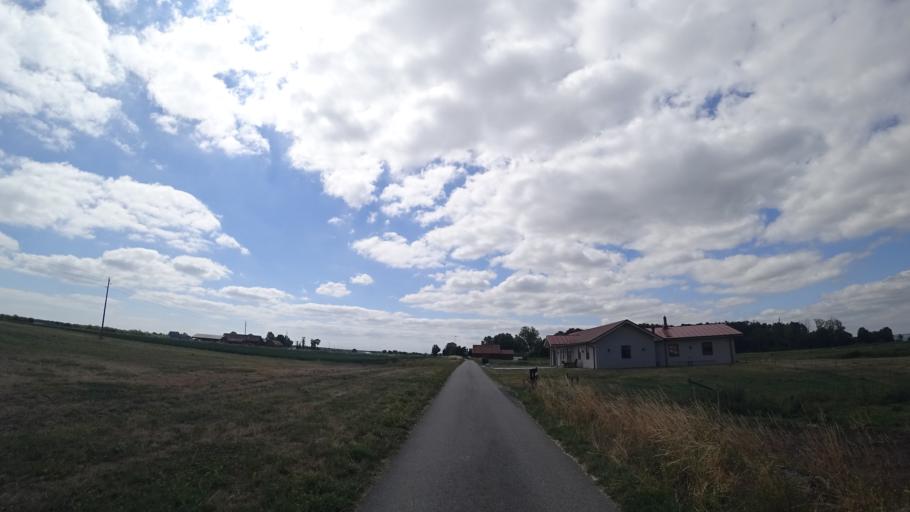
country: SE
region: Skane
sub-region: Kristianstads Kommun
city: Ahus
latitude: 55.9746
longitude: 14.2641
